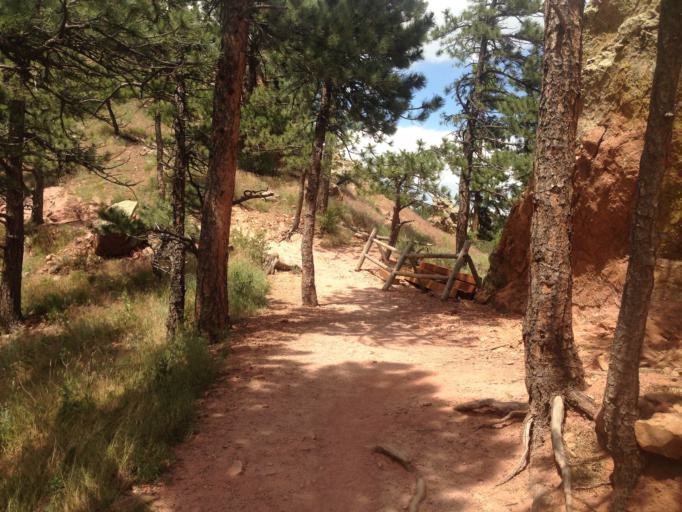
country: US
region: Colorado
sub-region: Boulder County
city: Boulder
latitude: 40.0237
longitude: -105.2987
